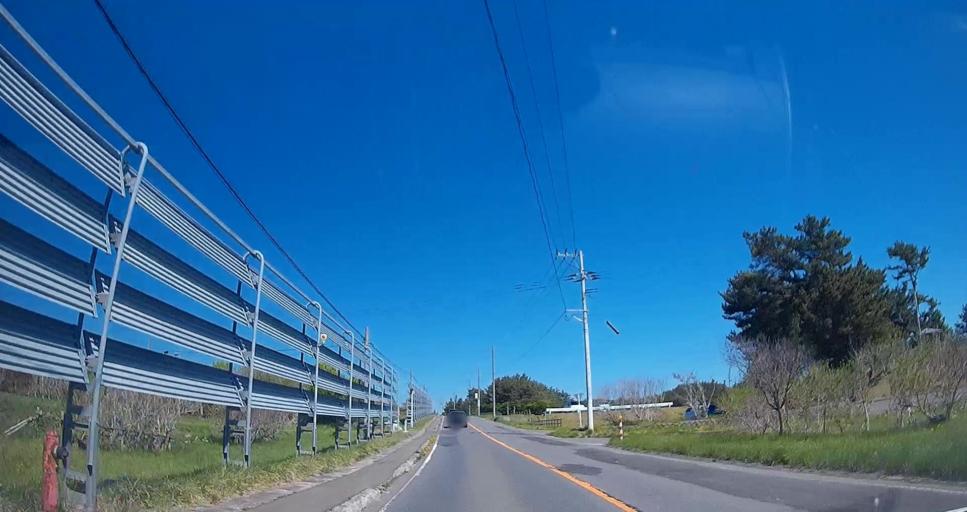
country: JP
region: Aomori
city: Misawa
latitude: 40.6984
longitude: 141.4235
